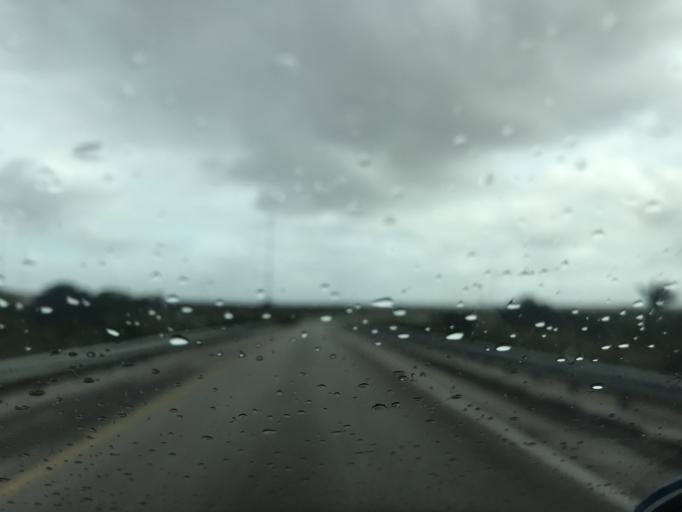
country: US
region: Florida
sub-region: Broward County
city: Weston
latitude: 26.1438
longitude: -80.4439
